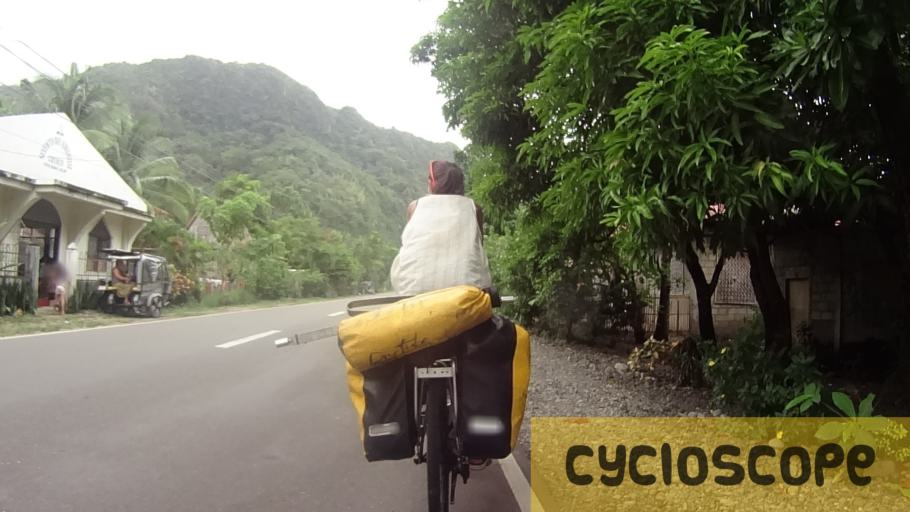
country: PH
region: Western Visayas
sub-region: Province of Aklan
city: Gibong
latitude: 11.8635
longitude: 122.0390
